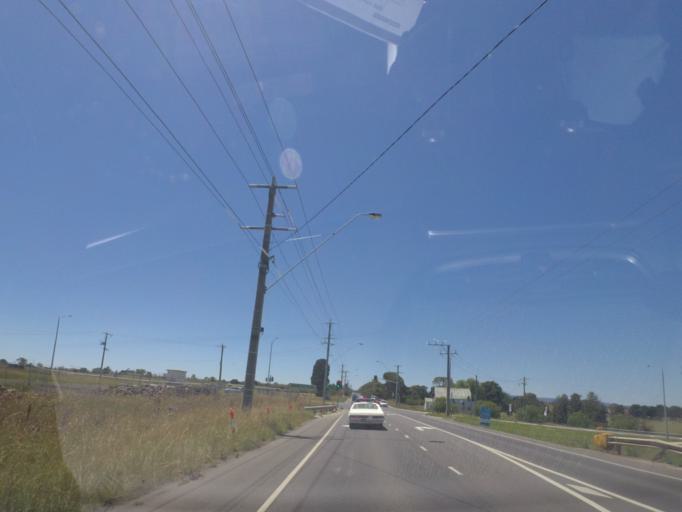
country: AU
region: Victoria
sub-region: Whittlesea
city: Epping
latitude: -37.6098
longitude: 145.0310
